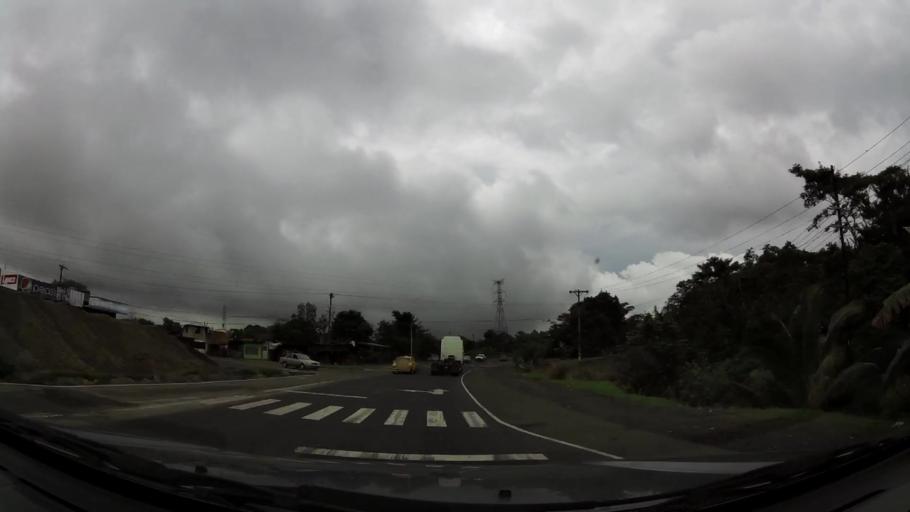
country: PA
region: Colon
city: Nuevo Vigia
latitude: 9.2016
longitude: -79.6259
